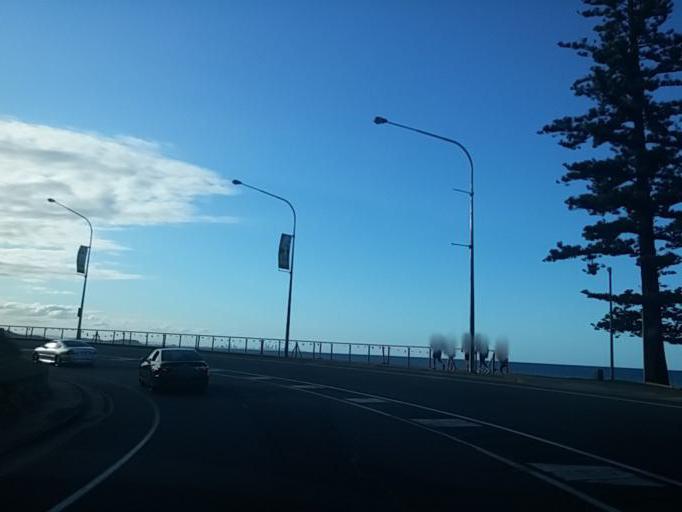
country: AU
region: New South Wales
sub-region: Tweed
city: Tweed Heads West
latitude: -28.1661
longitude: 153.5353
